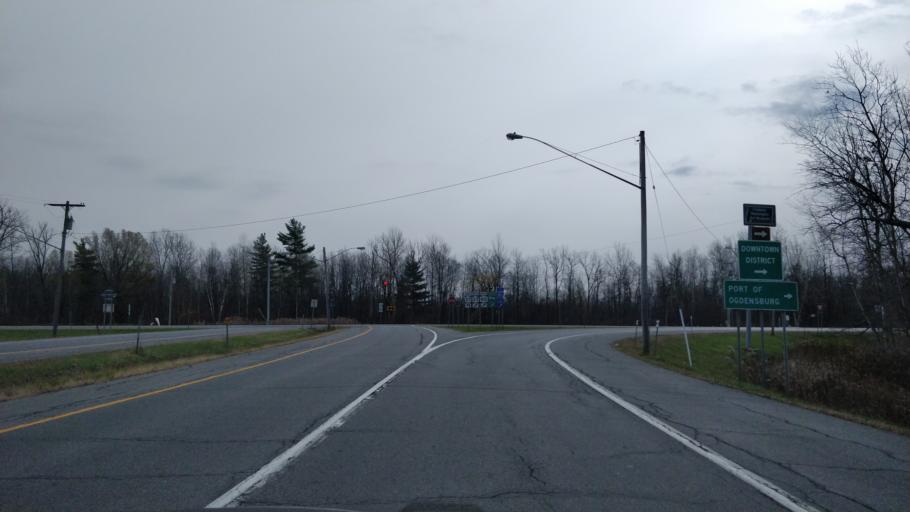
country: US
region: New York
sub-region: St. Lawrence County
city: Ogdensburg
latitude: 44.7140
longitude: -75.4504
